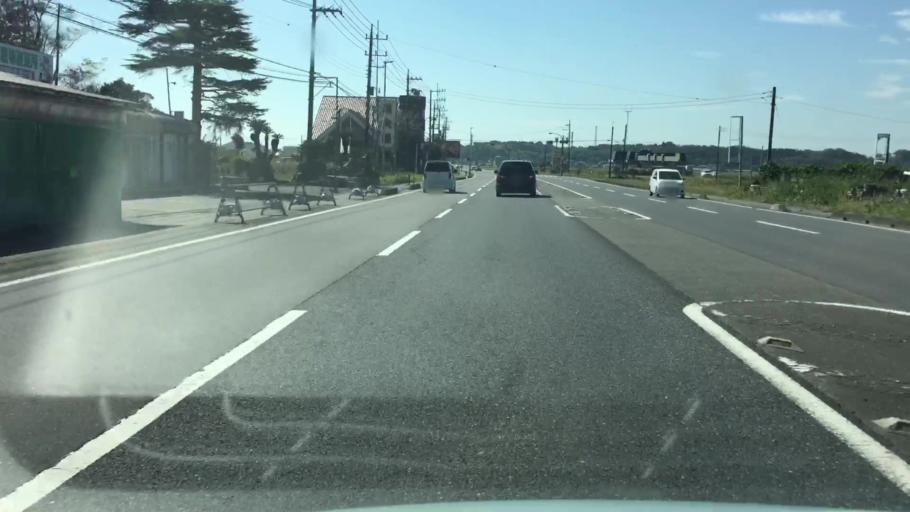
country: JP
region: Ibaraki
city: Ryugasaki
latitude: 35.8927
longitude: 140.1629
